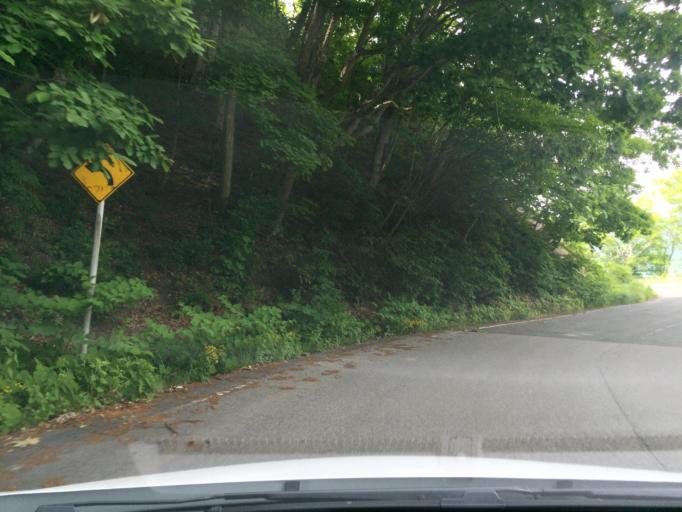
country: JP
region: Fukushima
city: Inawashiro
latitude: 37.7115
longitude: 140.0435
